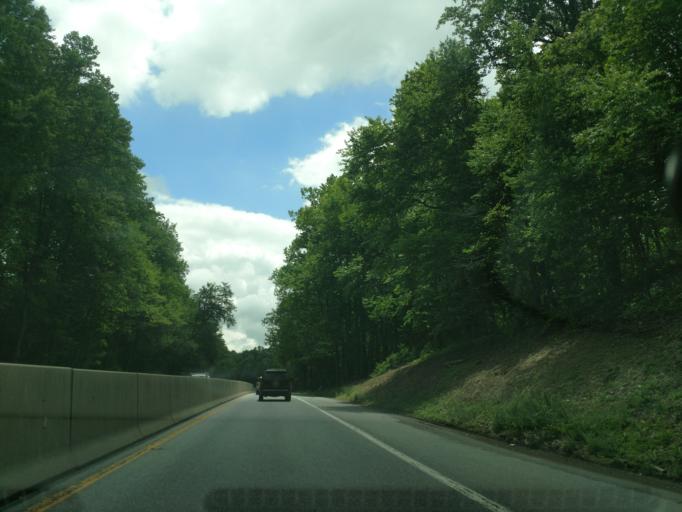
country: US
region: Pennsylvania
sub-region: Lebanon County
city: Cornwall
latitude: 40.2602
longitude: -76.4324
